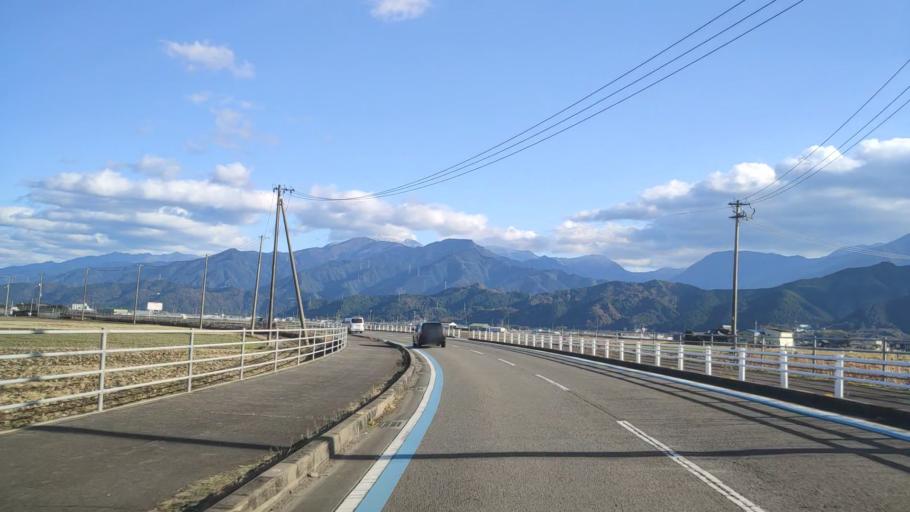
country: JP
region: Ehime
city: Saijo
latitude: 33.9074
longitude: 133.1433
